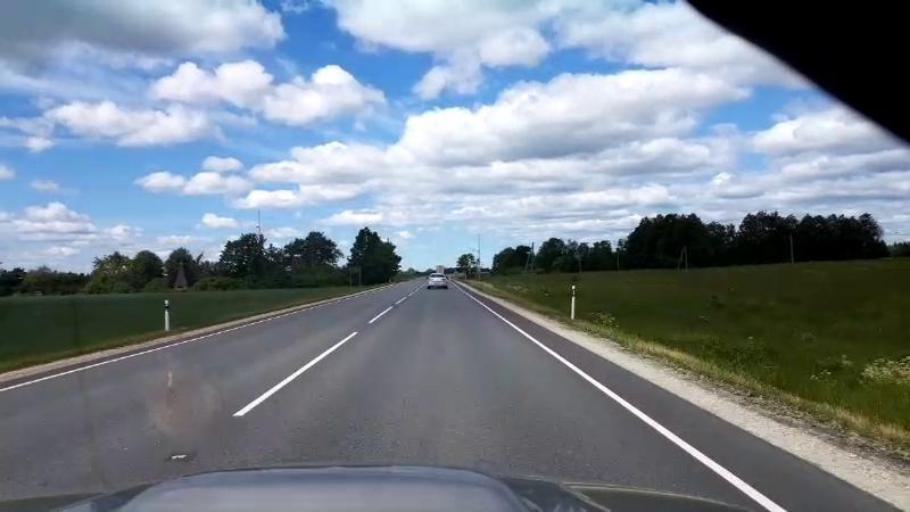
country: EE
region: Paernumaa
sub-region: Halinga vald
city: Parnu-Jaagupi
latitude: 58.6892
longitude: 24.4361
